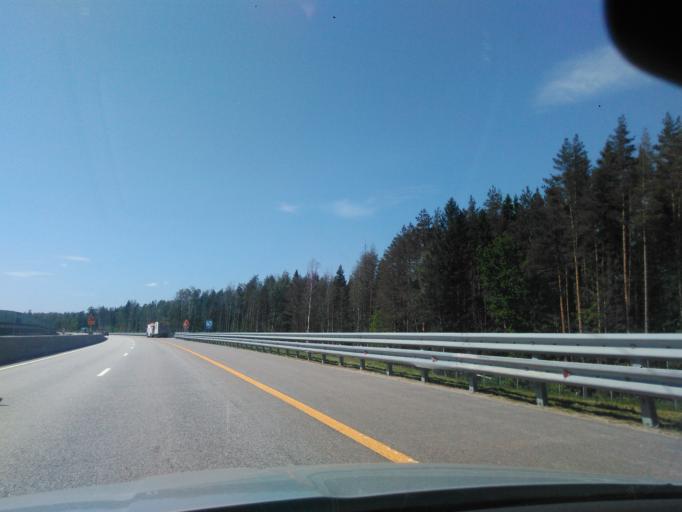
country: RU
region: Moskovskaya
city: Peshki
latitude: 56.1393
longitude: 37.0937
